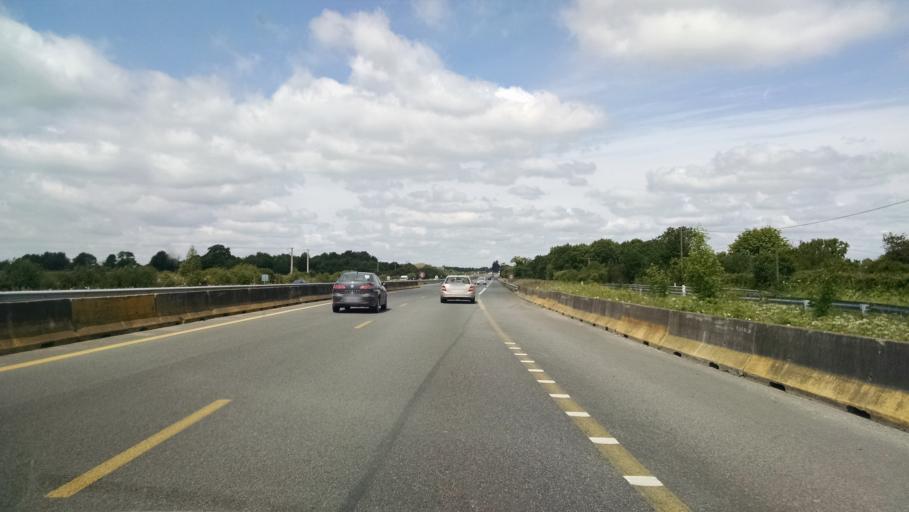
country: FR
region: Pays de la Loire
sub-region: Departement de la Loire-Atlantique
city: Malville
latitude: 47.3500
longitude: -1.8752
